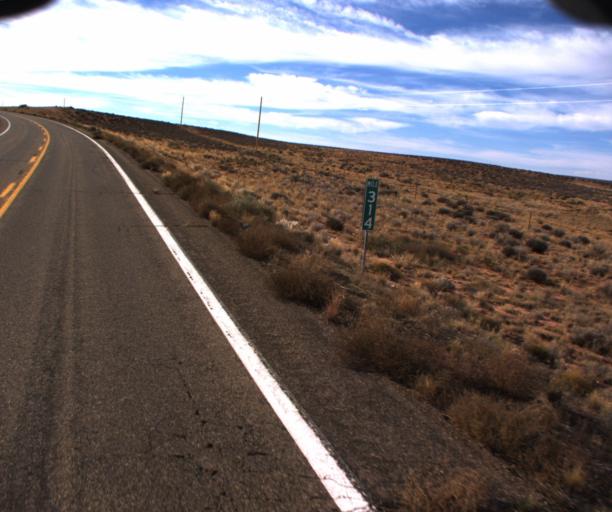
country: US
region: Arizona
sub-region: Coconino County
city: LeChee
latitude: 36.7350
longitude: -111.2845
